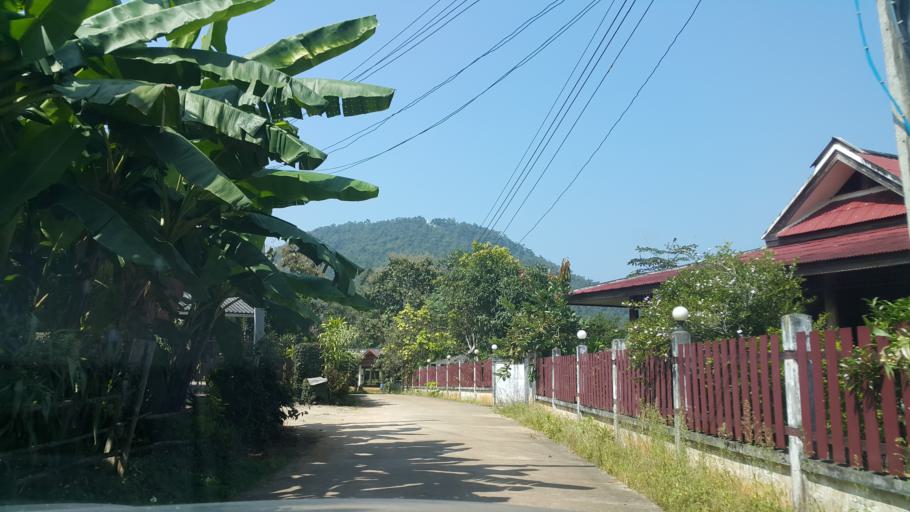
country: TH
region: Chiang Mai
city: Samoeng
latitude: 18.8515
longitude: 98.6993
